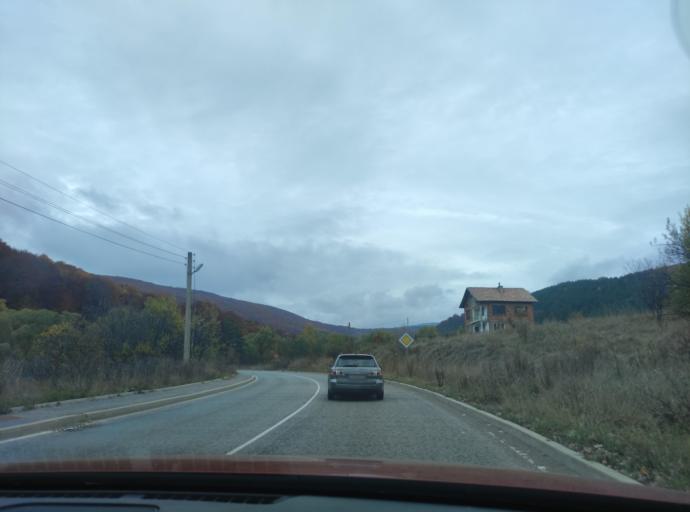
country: BG
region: Sofiya
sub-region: Obshtina Godech
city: Godech
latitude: 43.0808
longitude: 23.1060
